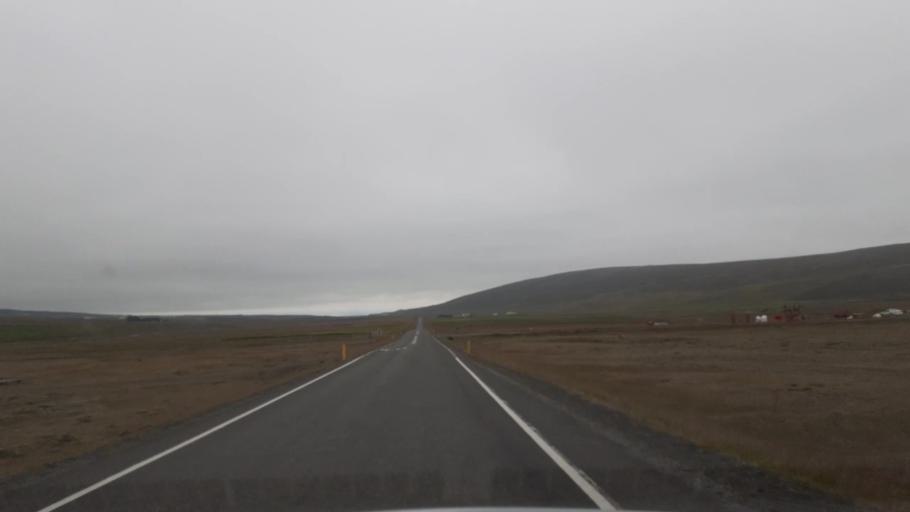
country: IS
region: Northeast
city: Siglufjoerdur
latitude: 65.7403
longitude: -19.1398
